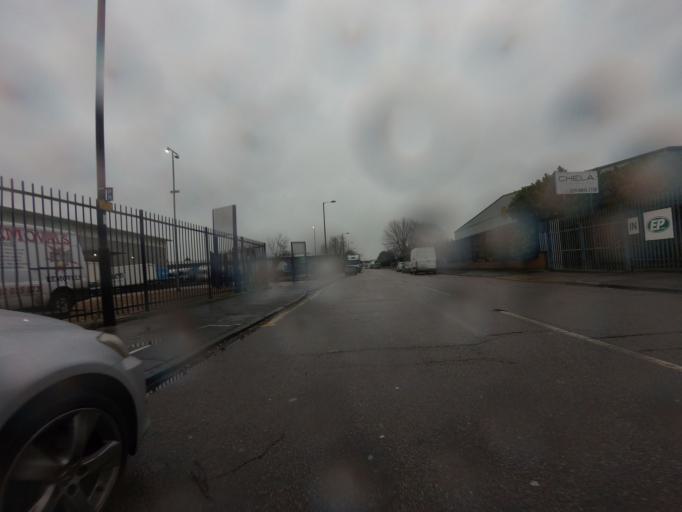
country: GB
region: England
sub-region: Hertfordshire
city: Waltham Cross
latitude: 51.6647
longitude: -0.0276
